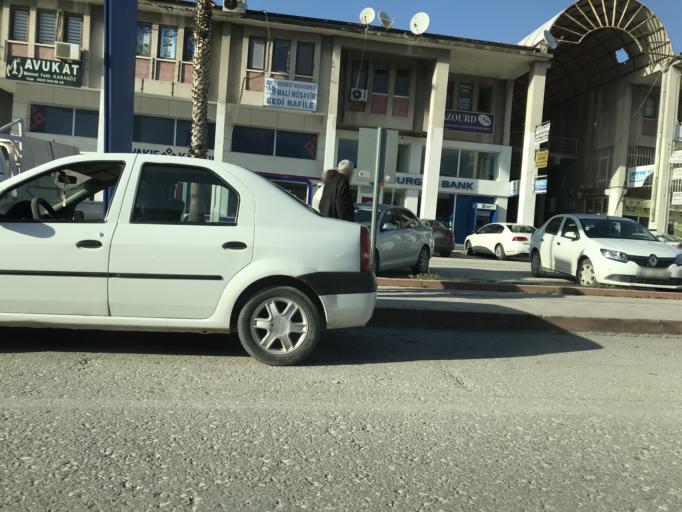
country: TR
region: Hatay
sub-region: Antakya Ilcesi
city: Antakya
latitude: 36.2083
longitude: 36.1672
